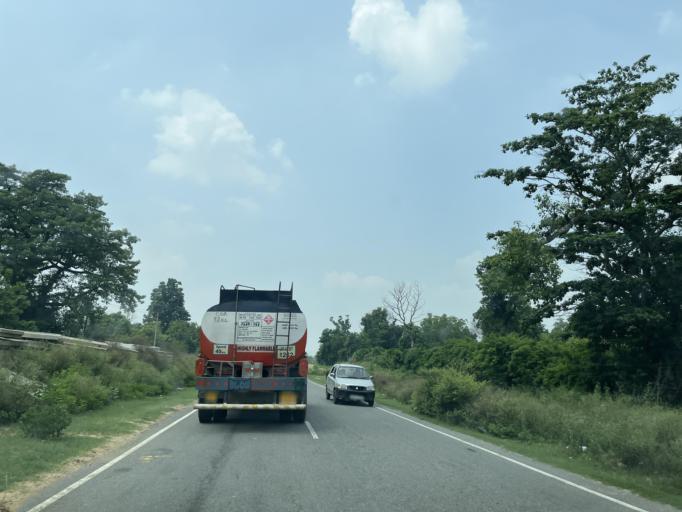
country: IN
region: Uttarakhand
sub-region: Haridwar
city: Haridwar
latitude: 29.8438
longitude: 78.1892
